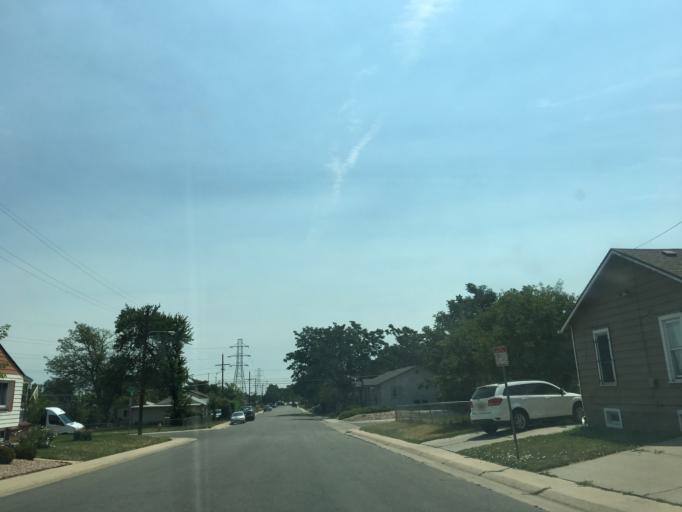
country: US
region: Colorado
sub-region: Jefferson County
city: Lakewood
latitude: 39.6985
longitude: -105.0386
